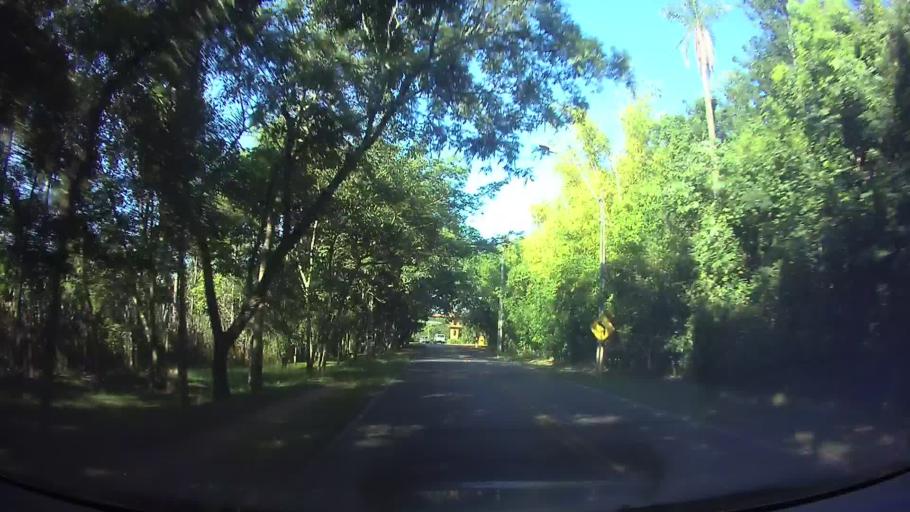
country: PY
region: Cordillera
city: Atyra
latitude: -25.2894
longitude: -57.1800
